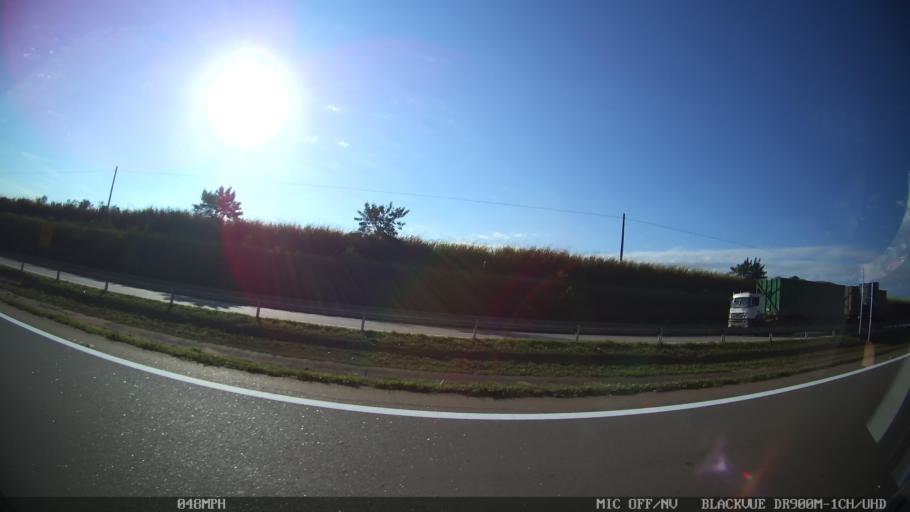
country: BR
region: Sao Paulo
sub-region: Piracicaba
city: Piracicaba
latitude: -22.6632
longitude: -47.6145
